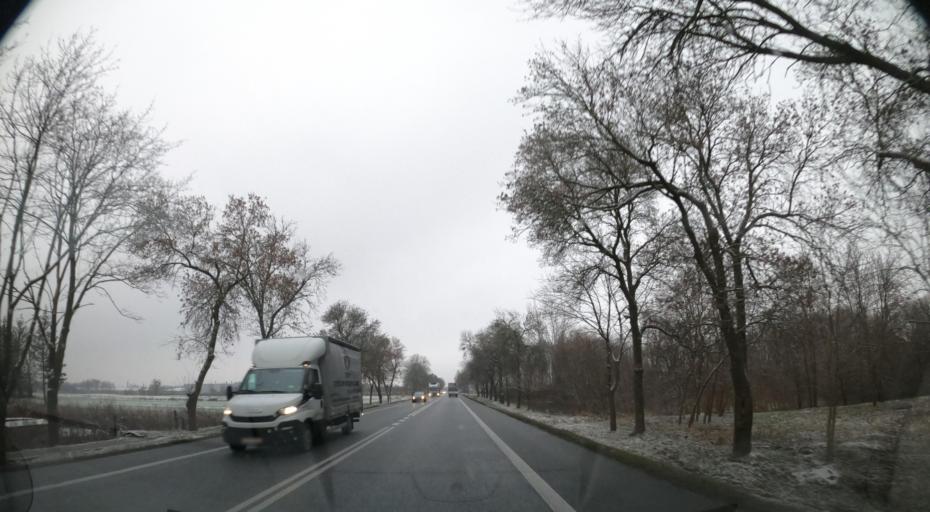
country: PL
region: Masovian Voivodeship
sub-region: Powiat warszawski zachodni
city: Bieniewice
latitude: 52.2032
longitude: 20.5252
